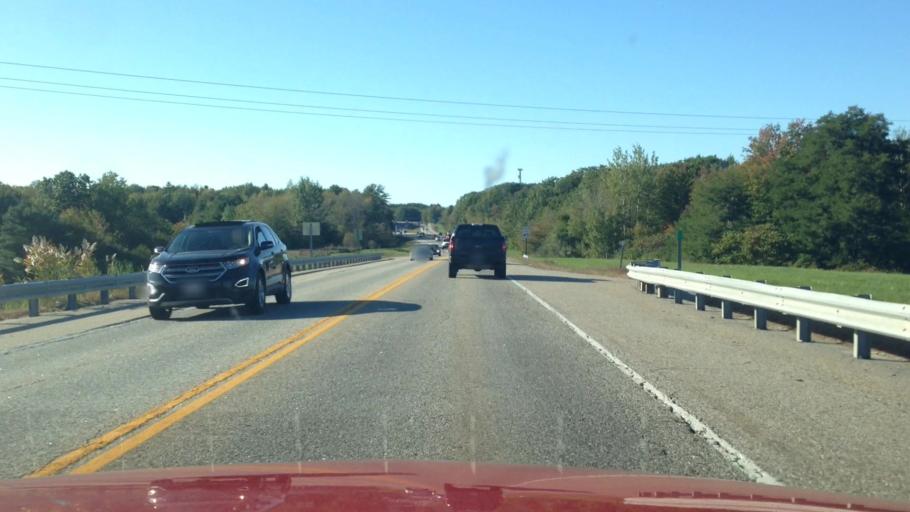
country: US
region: Maine
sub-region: Cumberland County
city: South Portland Gardens
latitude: 43.6679
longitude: -70.3320
